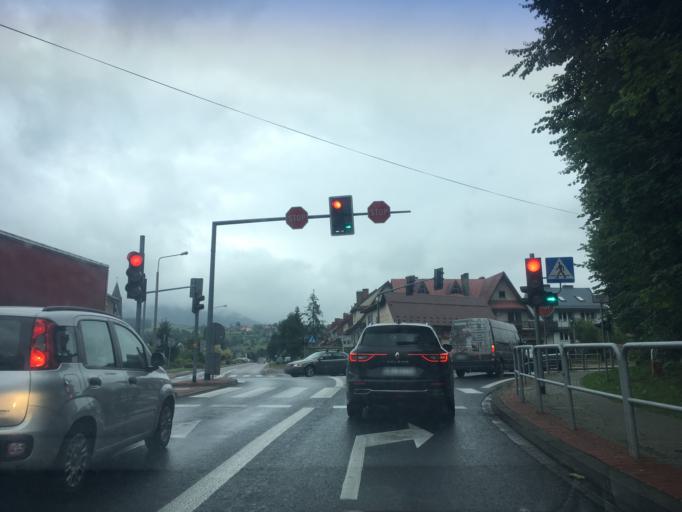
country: PL
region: Lesser Poland Voivodeship
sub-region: Powiat limanowski
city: Mszana Dolna
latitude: 49.6755
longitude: 20.0642
